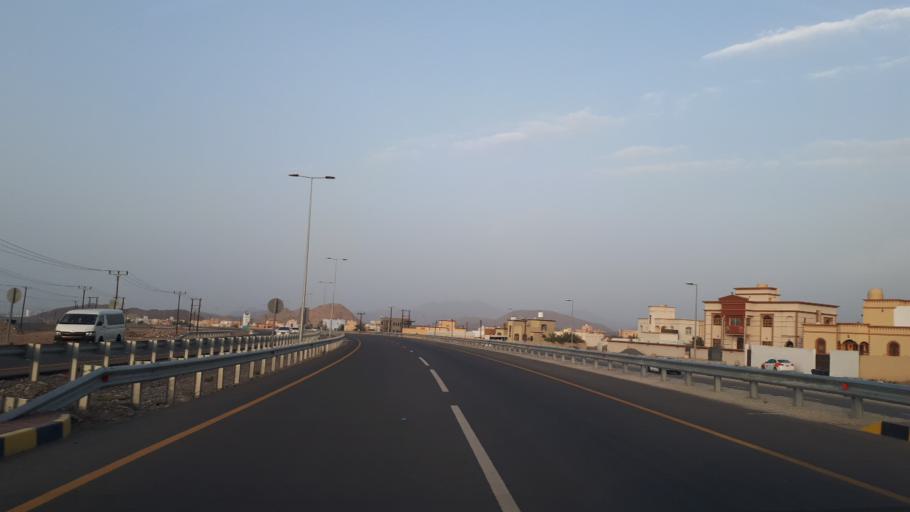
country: OM
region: Al Batinah
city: Rustaq
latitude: 23.4105
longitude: 57.3512
